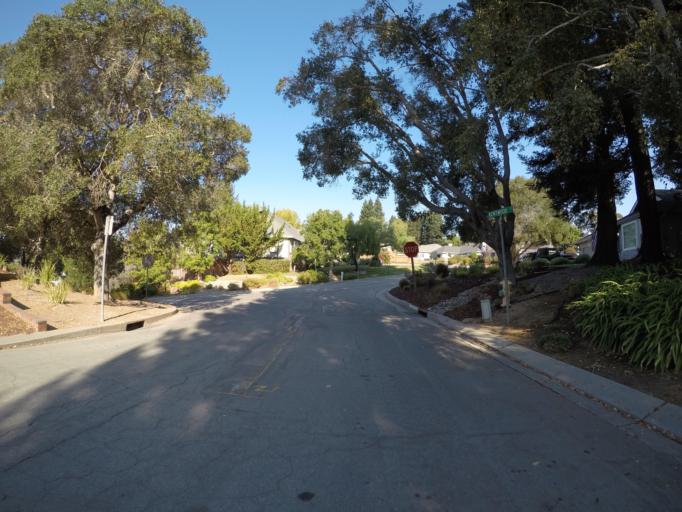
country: US
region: California
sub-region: Santa Cruz County
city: Scotts Valley
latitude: 37.0416
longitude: -122.0209
